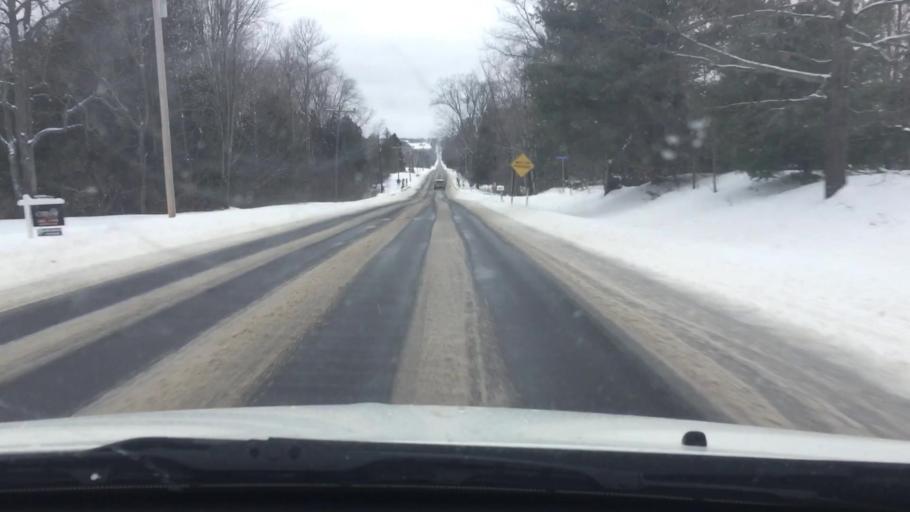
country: US
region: Michigan
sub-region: Charlevoix County
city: East Jordan
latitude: 45.1326
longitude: -85.1222
